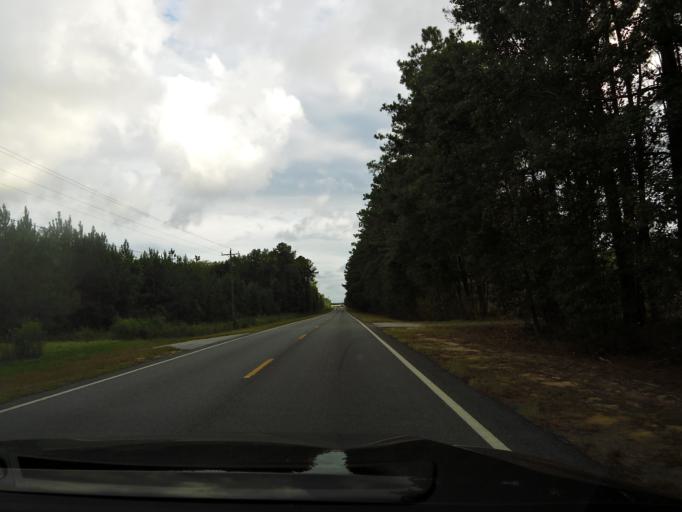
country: US
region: Georgia
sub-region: Liberty County
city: Midway
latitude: 31.6673
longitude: -81.4001
